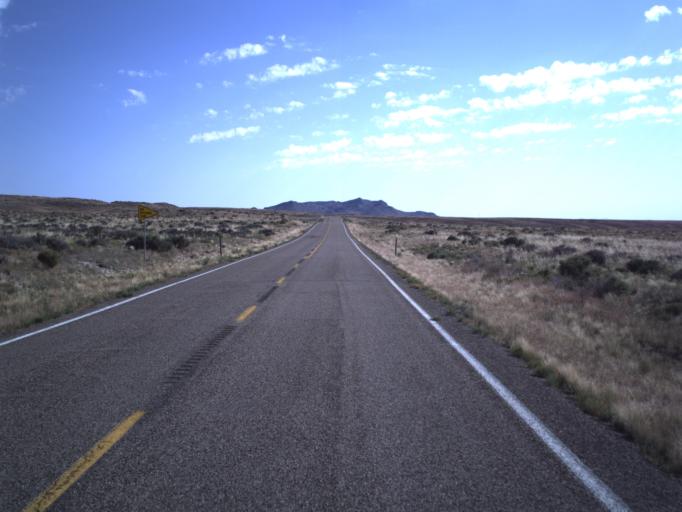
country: US
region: Utah
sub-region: Beaver County
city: Milford
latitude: 38.7585
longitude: -112.9434
